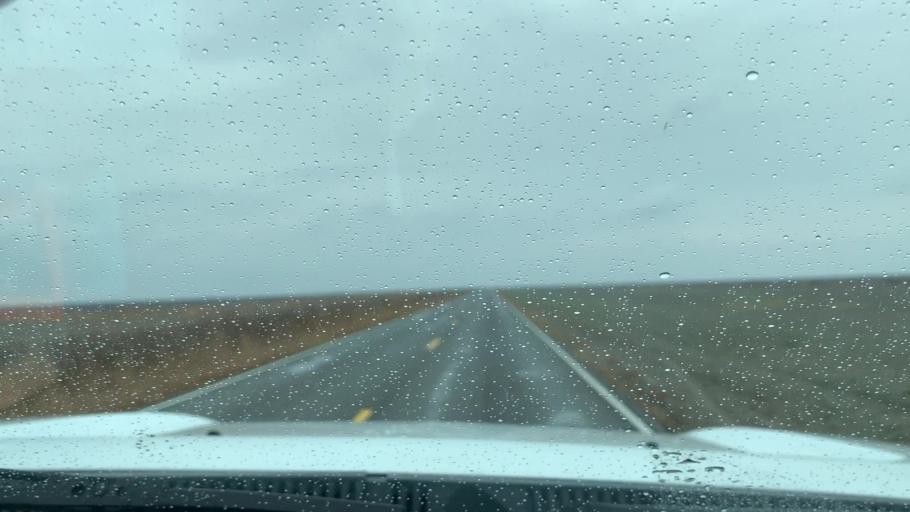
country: US
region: California
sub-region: Tulare County
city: Alpaugh
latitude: 35.9339
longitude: -119.6535
